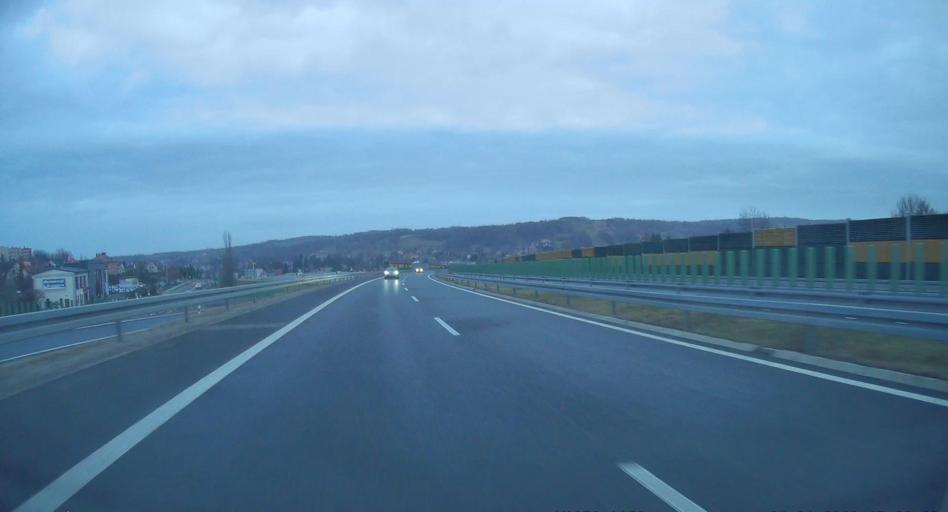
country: PL
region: Subcarpathian Voivodeship
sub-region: Powiat ropczycko-sedziszowski
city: Ropczyce
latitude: 50.0560
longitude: 21.5962
